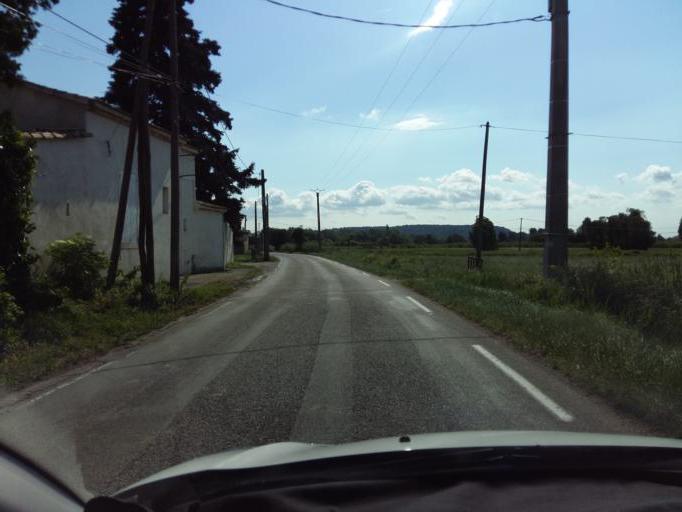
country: FR
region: Provence-Alpes-Cote d'Azur
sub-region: Departement du Vaucluse
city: Taillades
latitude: 43.8527
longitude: 5.0713
